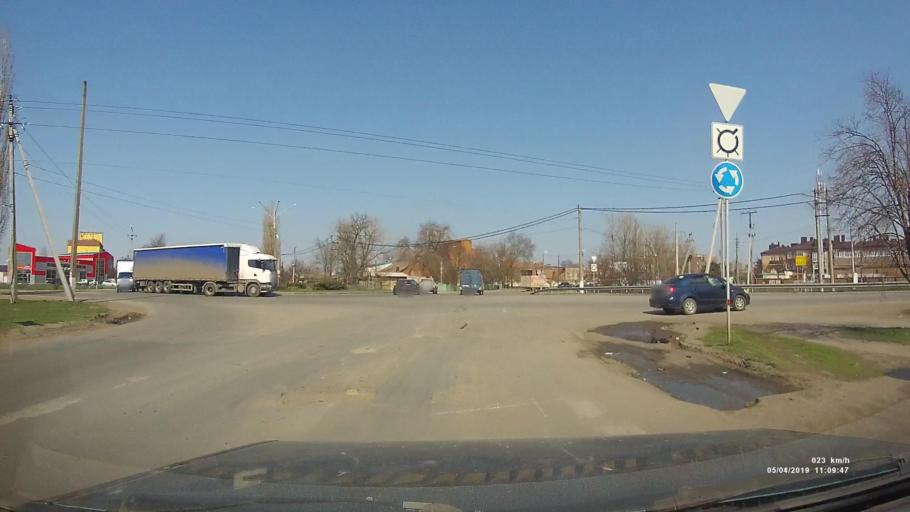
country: RU
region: Rostov
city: Azov
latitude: 47.0915
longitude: 39.4323
